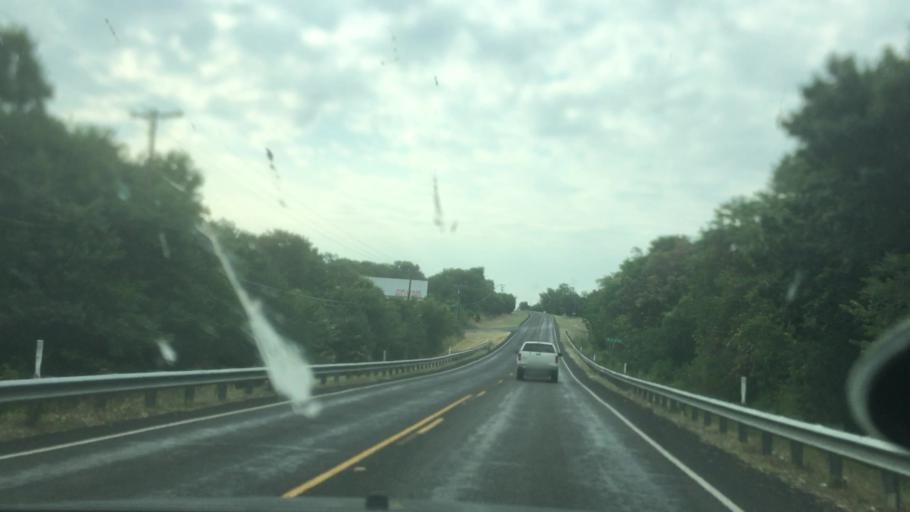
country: US
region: Texas
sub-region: Grayson County
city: Pottsboro
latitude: 33.7914
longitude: -96.6078
